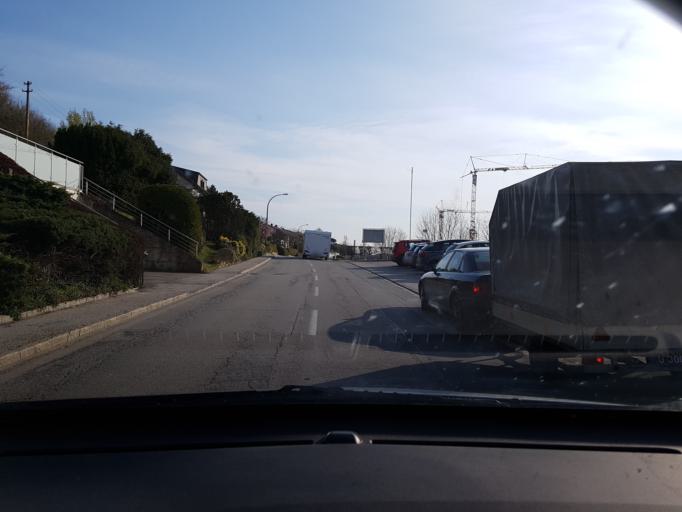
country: AT
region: Upper Austria
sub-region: Politischer Bezirk Linz-Land
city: Sankt Florian
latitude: 48.2088
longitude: 14.3906
